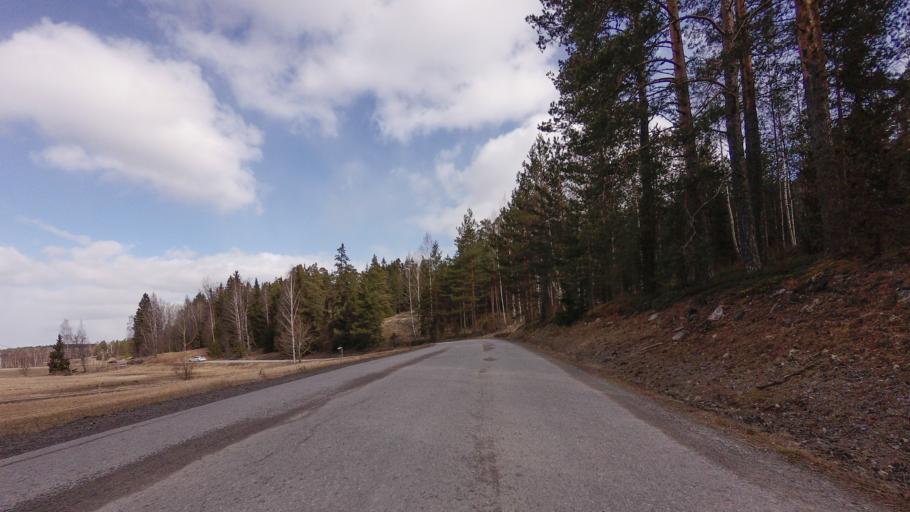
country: FI
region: Uusimaa
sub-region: Helsinki
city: Karjalohja
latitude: 60.2671
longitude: 23.6683
